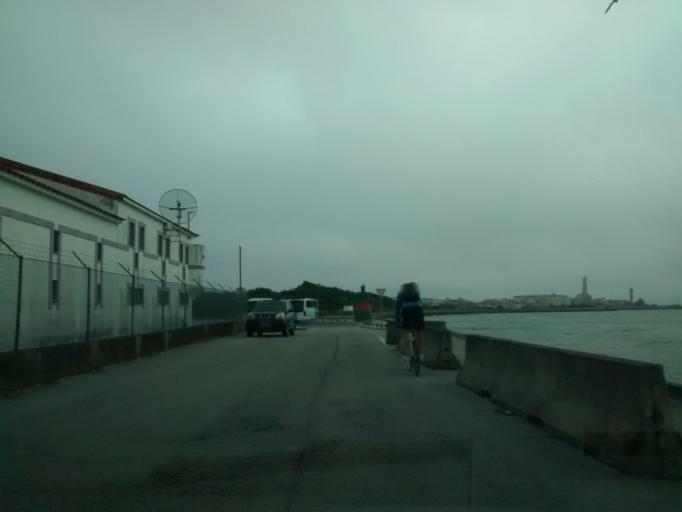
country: PT
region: Aveiro
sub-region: Ilhavo
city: Gafanha da Nazare
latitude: 40.6480
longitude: -8.7341
